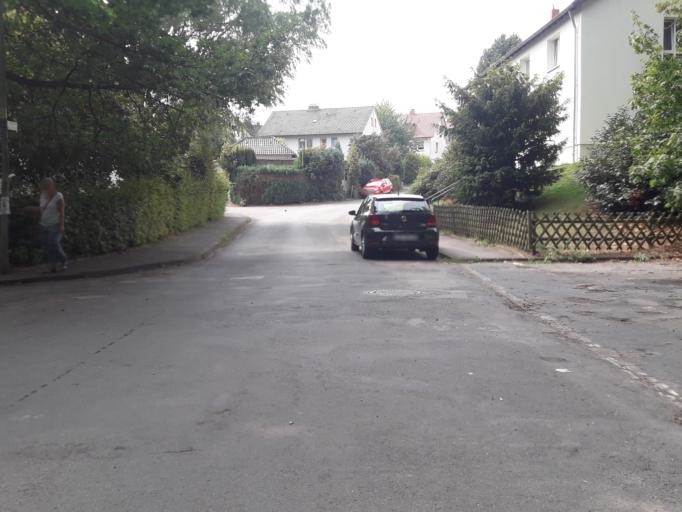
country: DE
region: North Rhine-Westphalia
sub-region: Regierungsbezirk Detmold
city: Detmold
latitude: 51.9237
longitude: 8.8949
